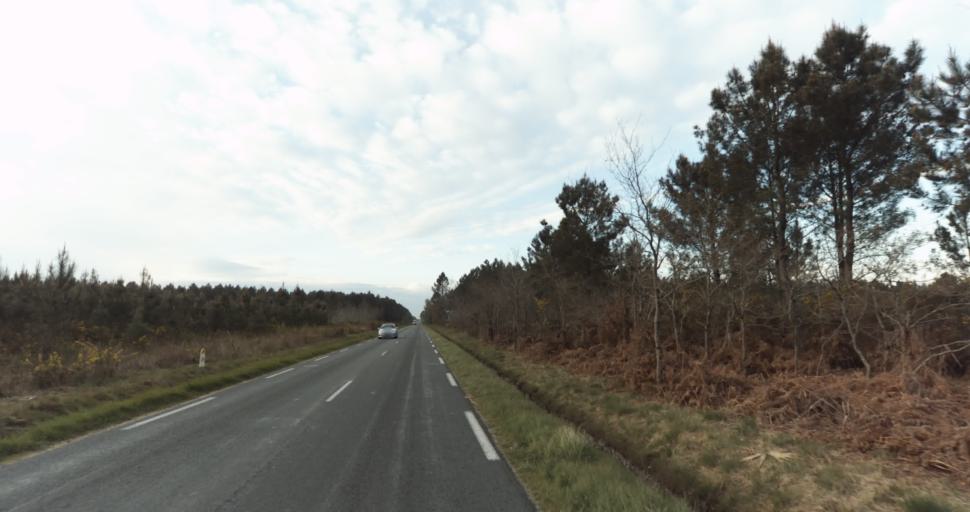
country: FR
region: Aquitaine
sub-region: Departement de la Gironde
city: Martignas-sur-Jalle
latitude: 44.7916
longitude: -0.7761
